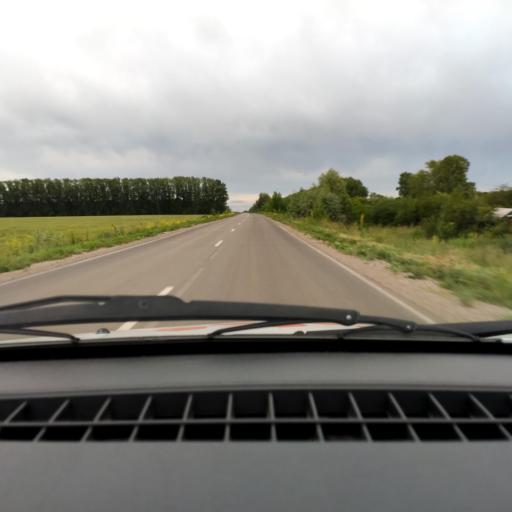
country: RU
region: Bashkortostan
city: Avdon
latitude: 54.5370
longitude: 55.7630
